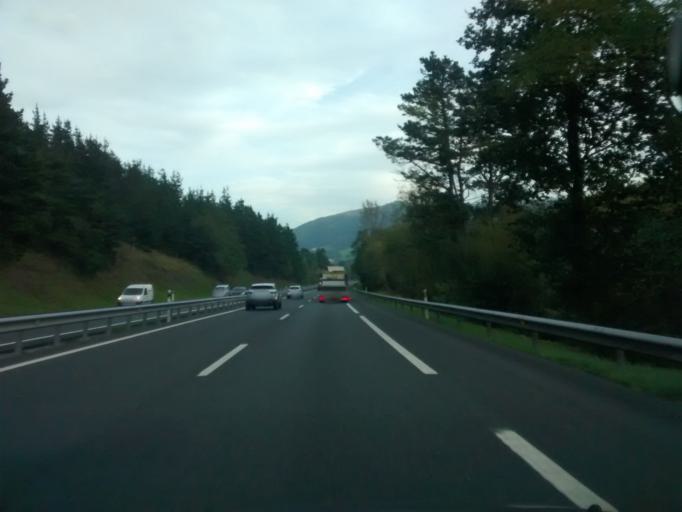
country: ES
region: Basque Country
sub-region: Provincia de Guipuzcoa
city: Deba
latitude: 43.2697
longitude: -2.3048
